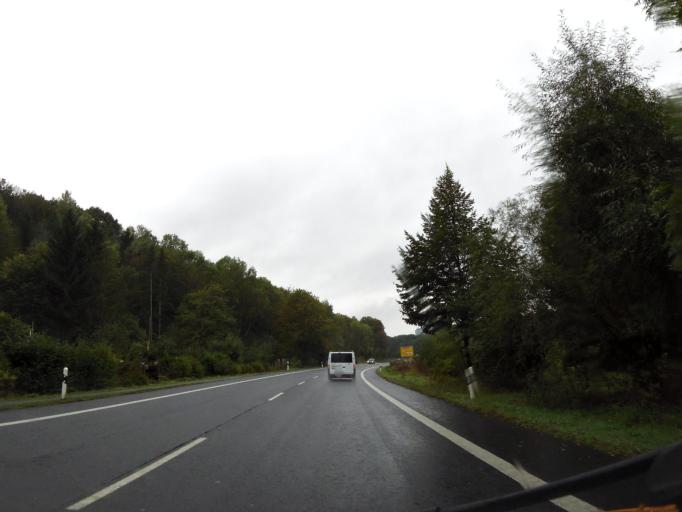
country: DE
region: Lower Saxony
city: Goettingen
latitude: 51.5514
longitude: 9.9699
